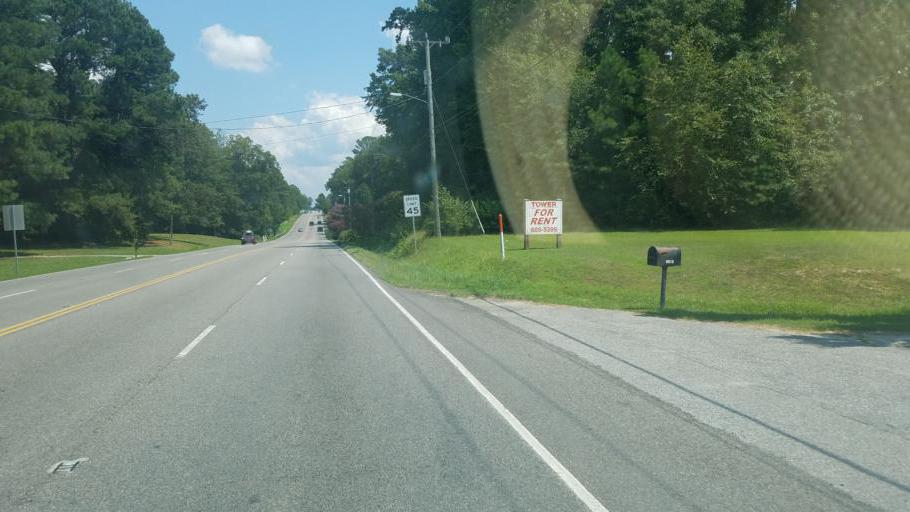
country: US
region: Virginia
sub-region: Isle of Wight County
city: Windsor
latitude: 36.8035
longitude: -76.7248
